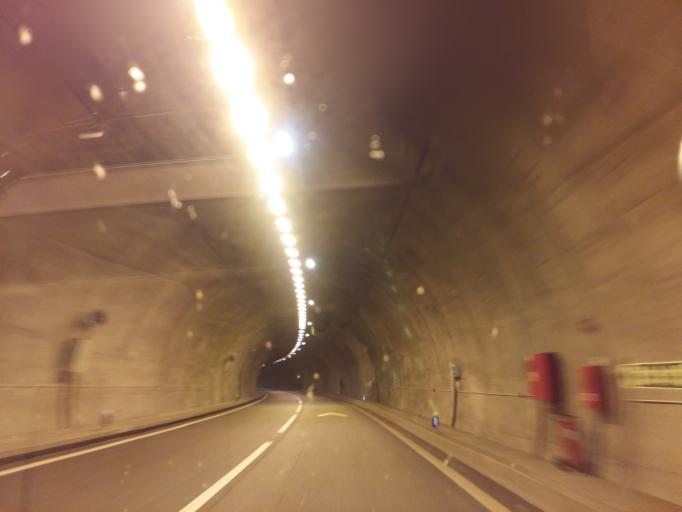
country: PT
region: Castelo Branco
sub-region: Concelho do Fundao
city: Fundao
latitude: 40.1049
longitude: -7.4697
